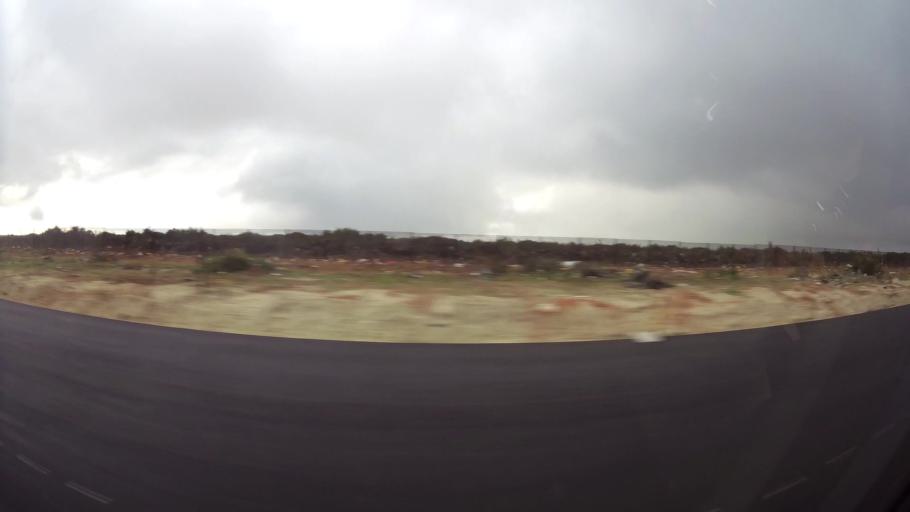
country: ZA
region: Eastern Cape
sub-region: Nelson Mandela Bay Metropolitan Municipality
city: Port Elizabeth
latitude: -33.8302
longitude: 25.5138
